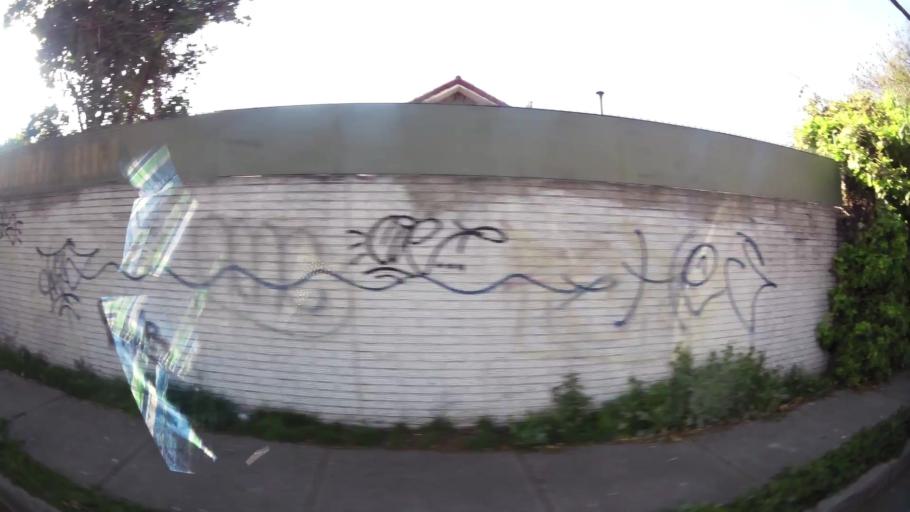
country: CL
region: Santiago Metropolitan
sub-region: Provincia de Santiago
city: Lo Prado
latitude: -33.4845
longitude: -70.7501
